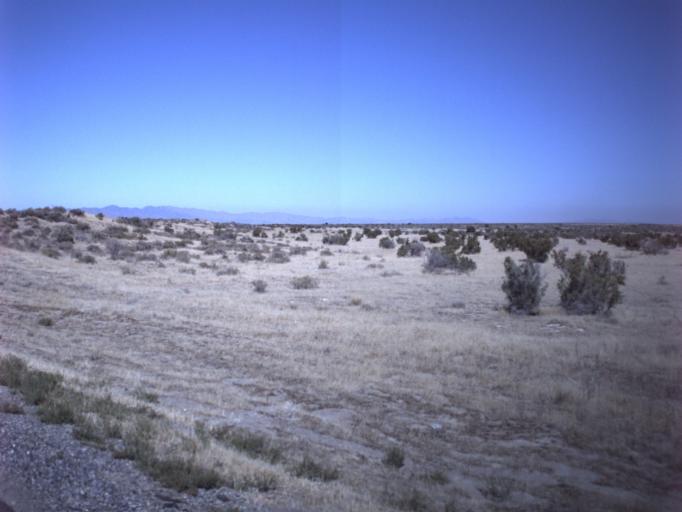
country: US
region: Utah
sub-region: Tooele County
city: Grantsville
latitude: 40.2485
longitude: -112.7276
